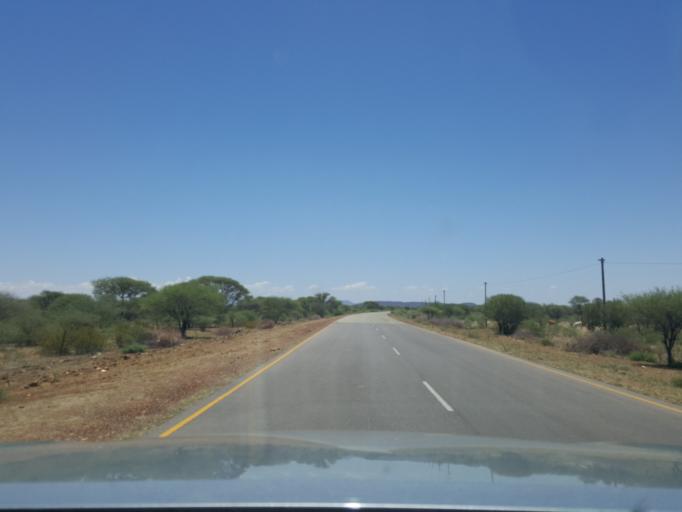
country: BW
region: South East
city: Ramotswa
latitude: -25.0260
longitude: 25.9173
